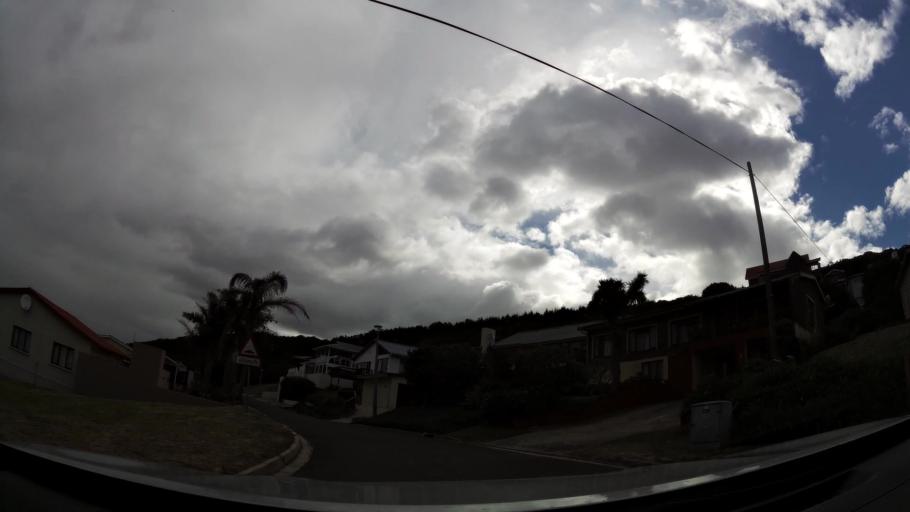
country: ZA
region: Western Cape
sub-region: Eden District Municipality
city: George
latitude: -34.0480
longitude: 22.3150
